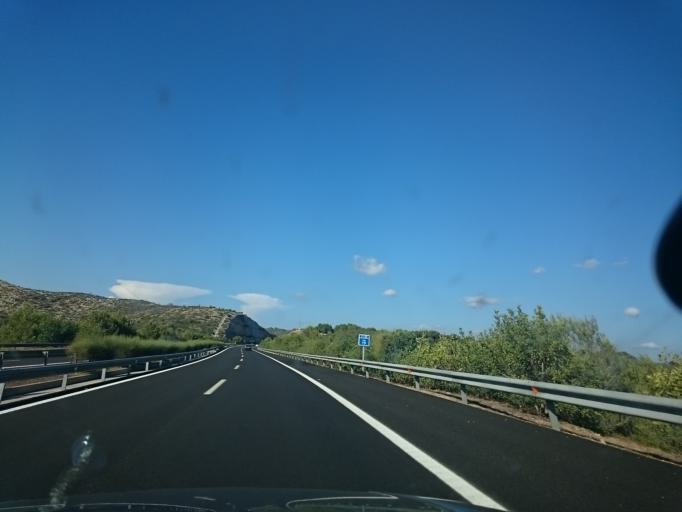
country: ES
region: Catalonia
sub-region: Provincia de Barcelona
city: Vilanova i la Geltru
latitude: 41.2442
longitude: 1.6903
